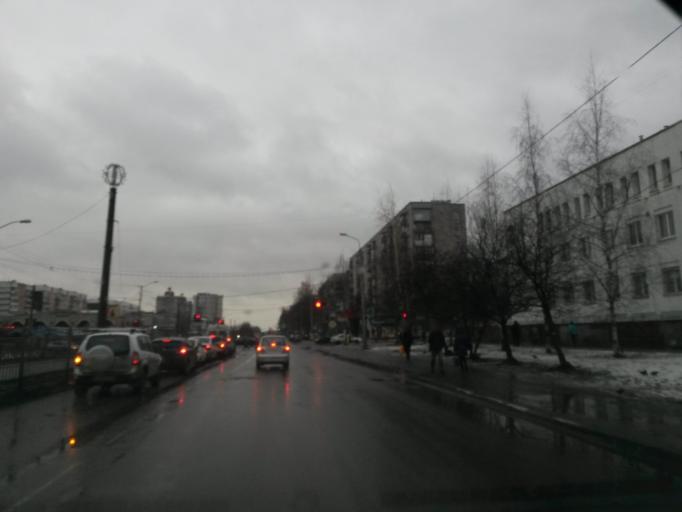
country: RU
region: Jaroslavl
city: Yaroslavl
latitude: 57.6509
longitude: 39.9480
